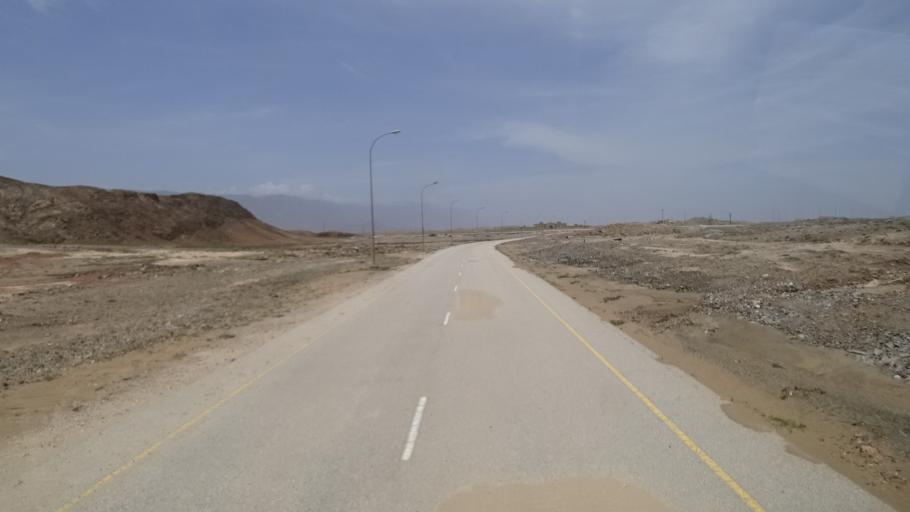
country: OM
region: Zufar
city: Salalah
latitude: 17.0074
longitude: 54.6937
